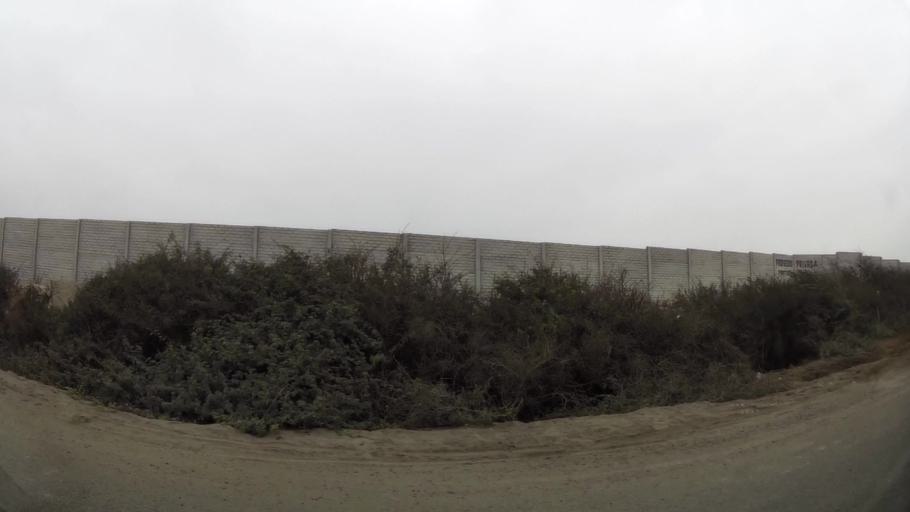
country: PE
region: Lima
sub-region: Lima
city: Punta Hermosa
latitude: -12.3251
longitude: -76.8335
